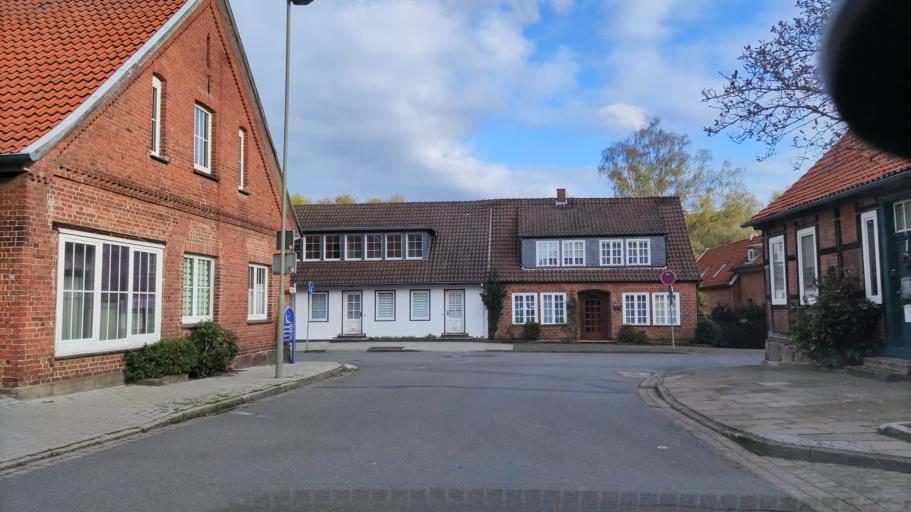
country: DE
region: Lower Saxony
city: Bad Bevensen
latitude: 53.0787
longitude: 10.5814
